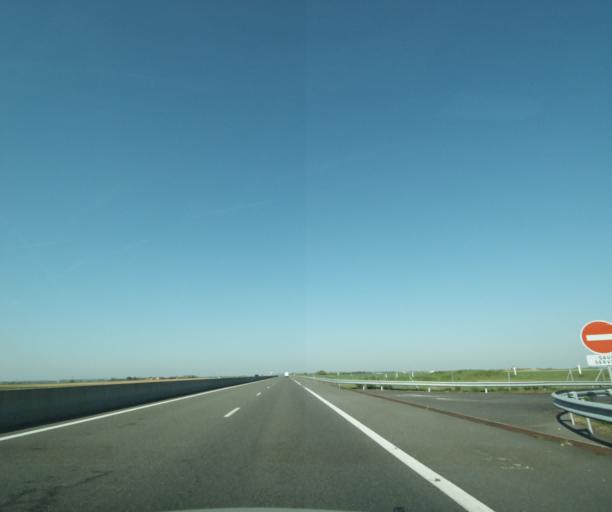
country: FR
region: Centre
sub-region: Departement du Loiret
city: Corbeilles
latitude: 48.0889
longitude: 2.5090
